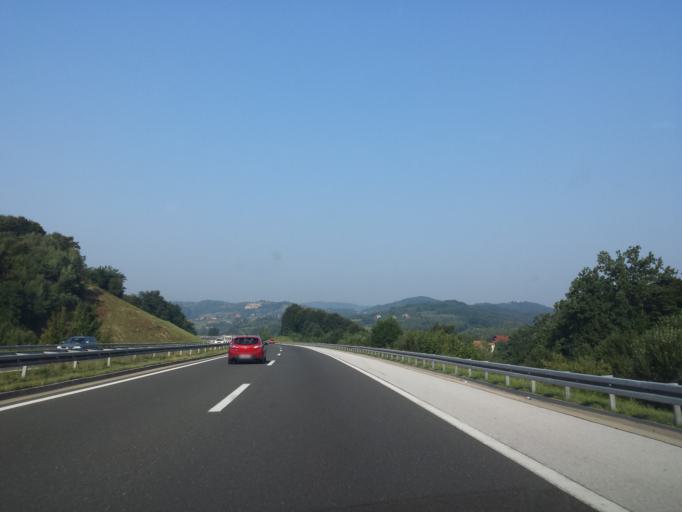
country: HR
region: Karlovacka
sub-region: Grad Karlovac
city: Karlovac
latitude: 45.5161
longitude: 15.4848
